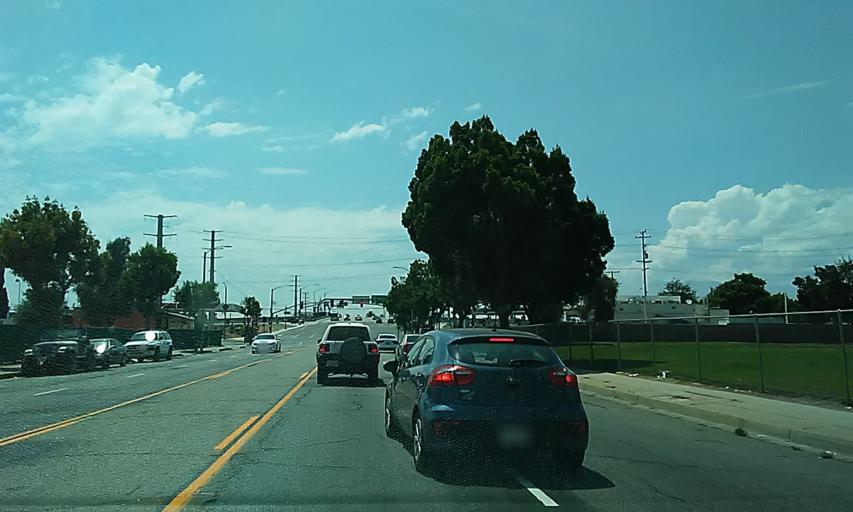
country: US
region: California
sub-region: San Bernardino County
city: San Bernardino
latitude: 34.1214
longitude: -117.2993
